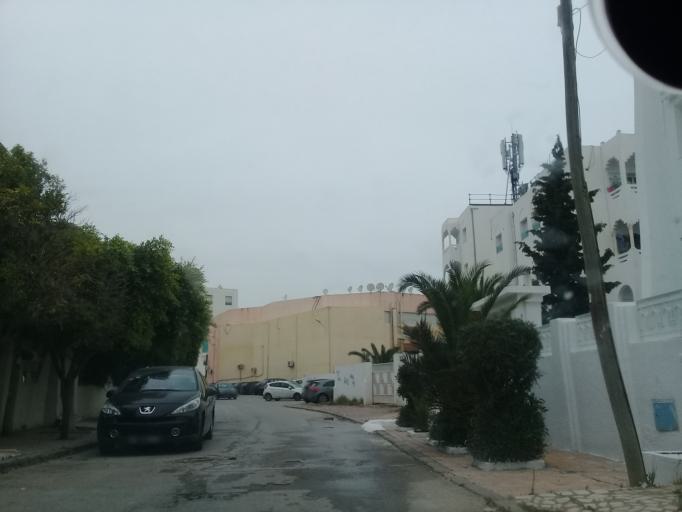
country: TN
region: Tunis
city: Tunis
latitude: 36.8442
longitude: 10.1531
